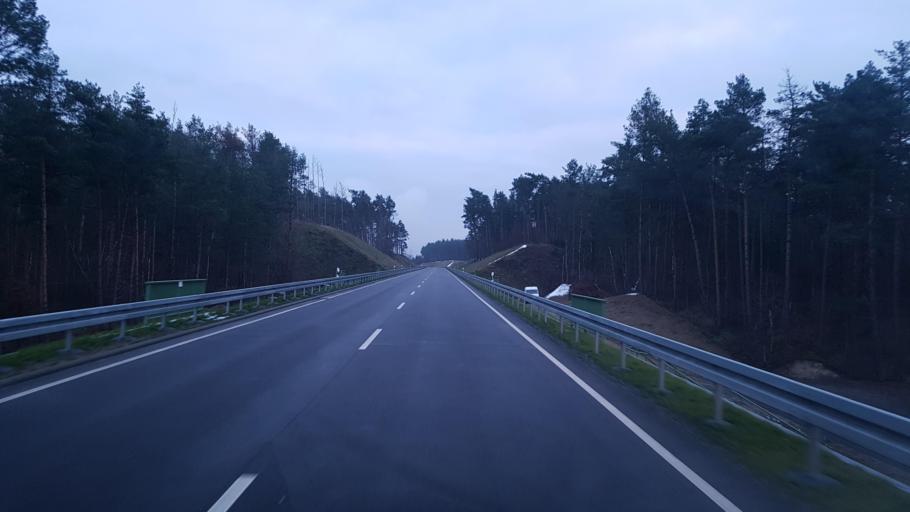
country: DE
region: Brandenburg
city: Wildau
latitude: 52.3196
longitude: 13.6585
